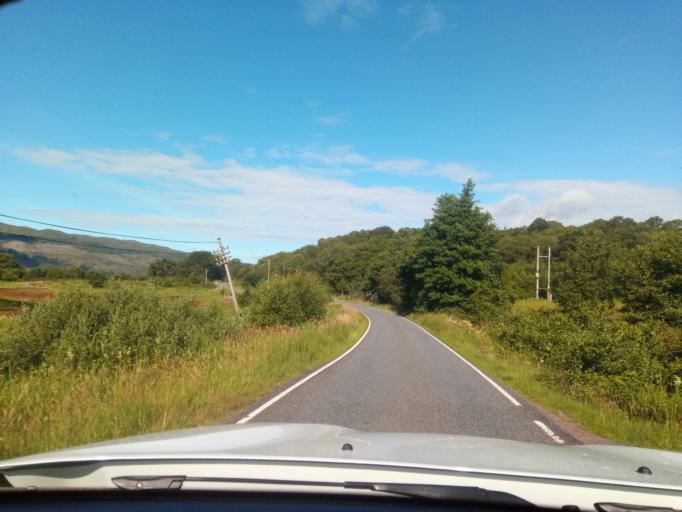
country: GB
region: Scotland
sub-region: Argyll and Bute
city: Isle Of Mull
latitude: 56.6887
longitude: -5.6633
